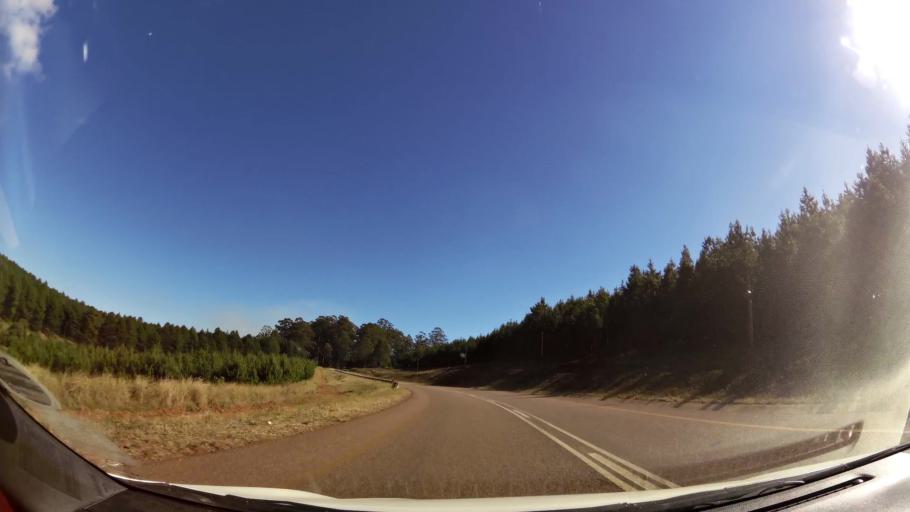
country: ZA
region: Limpopo
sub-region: Capricorn District Municipality
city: Mankoeng
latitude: -23.9123
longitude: 29.9651
